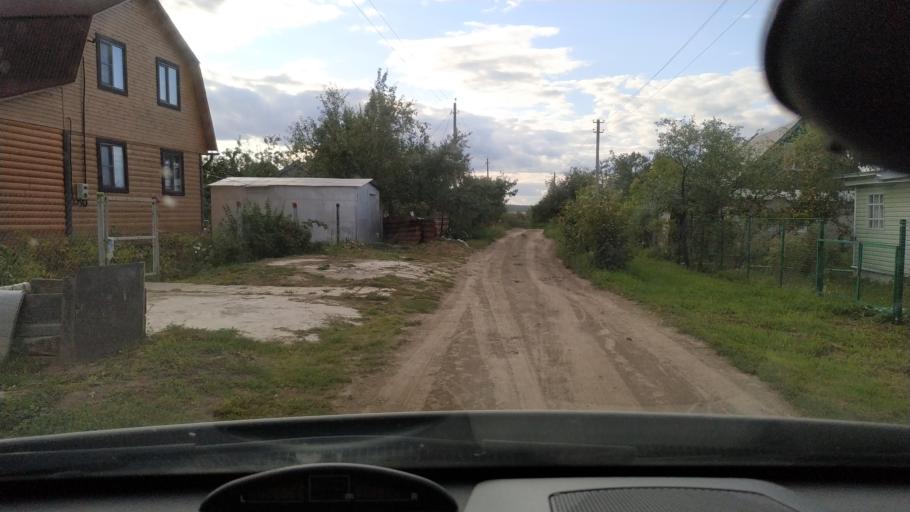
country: RU
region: Rjazan
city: Polyany
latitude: 54.5559
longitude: 39.8733
